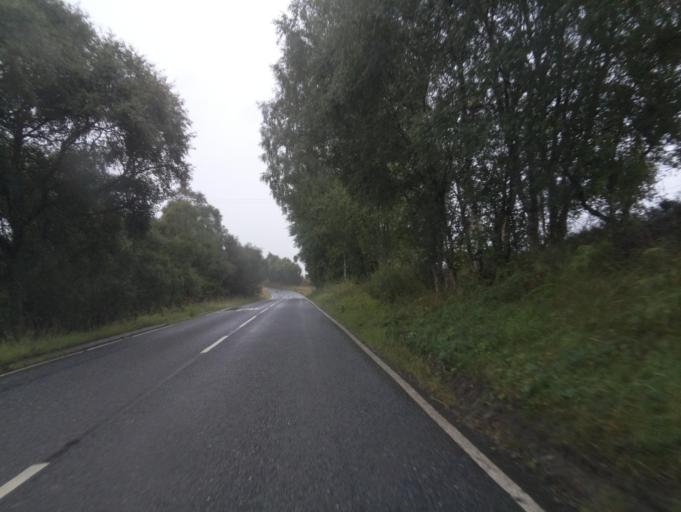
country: GB
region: Scotland
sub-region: Perth and Kinross
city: Blairgowrie
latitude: 56.6894
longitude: -3.4079
